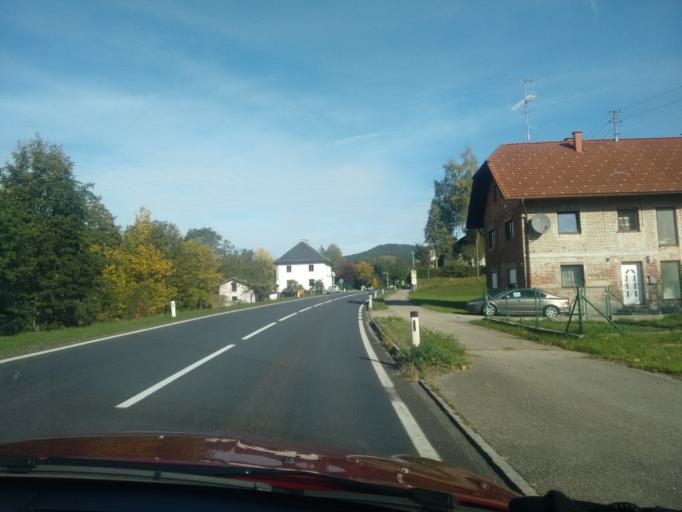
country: AT
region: Upper Austria
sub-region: Politischer Bezirk Vocklabruck
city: Zell am Pettenfirst
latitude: 48.0708
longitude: 13.5989
